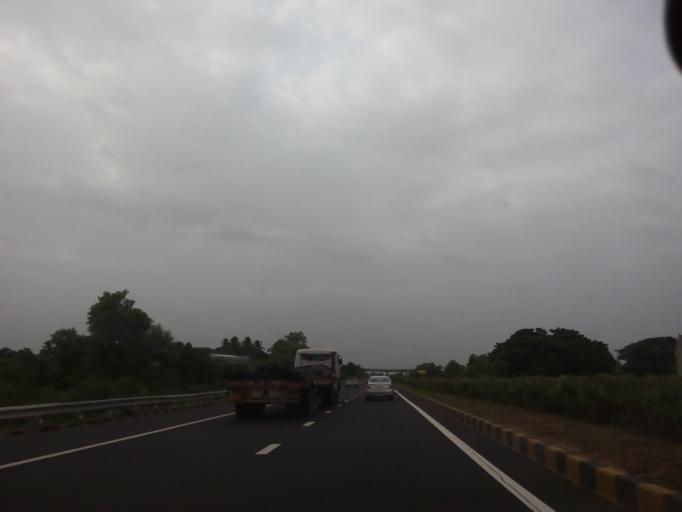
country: IN
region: Gujarat
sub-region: Kheda
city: Chaklasi
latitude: 22.6519
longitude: 72.9282
